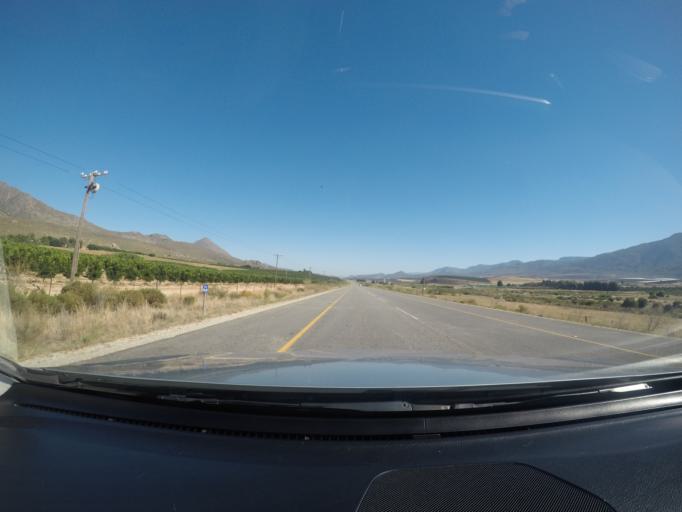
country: ZA
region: Western Cape
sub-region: West Coast District Municipality
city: Clanwilliam
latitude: -32.5685
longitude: 18.9864
